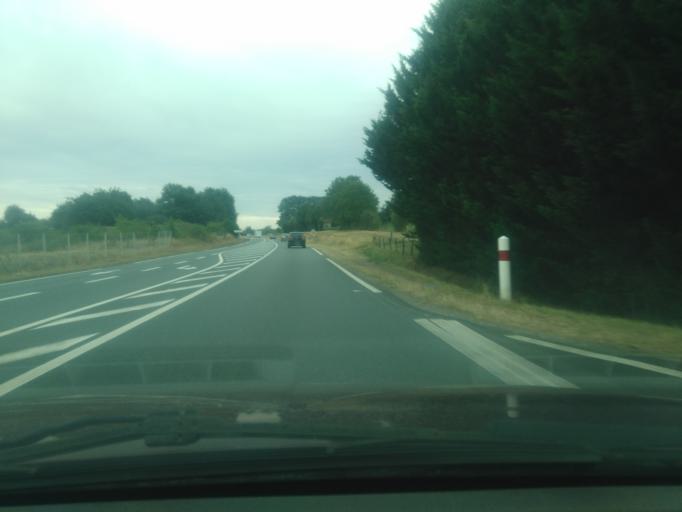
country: FR
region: Centre
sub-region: Departement de l'Indre
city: Saint-Gaultier
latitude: 46.6401
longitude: 1.4093
